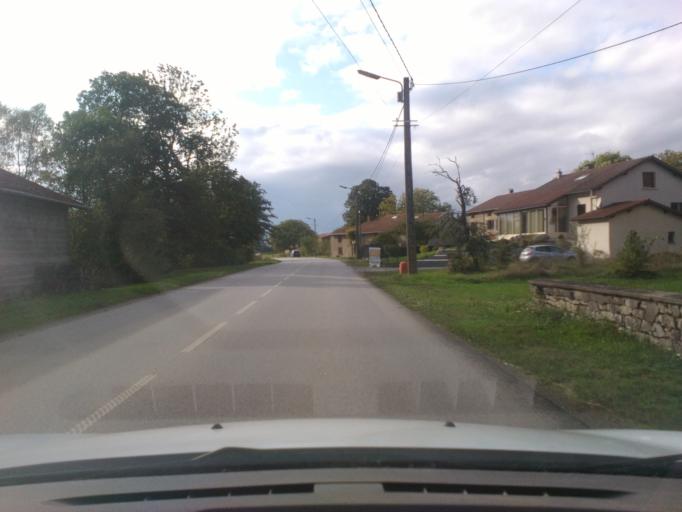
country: FR
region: Lorraine
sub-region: Departement des Vosges
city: Aydoilles
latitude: 48.2475
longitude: 6.6224
